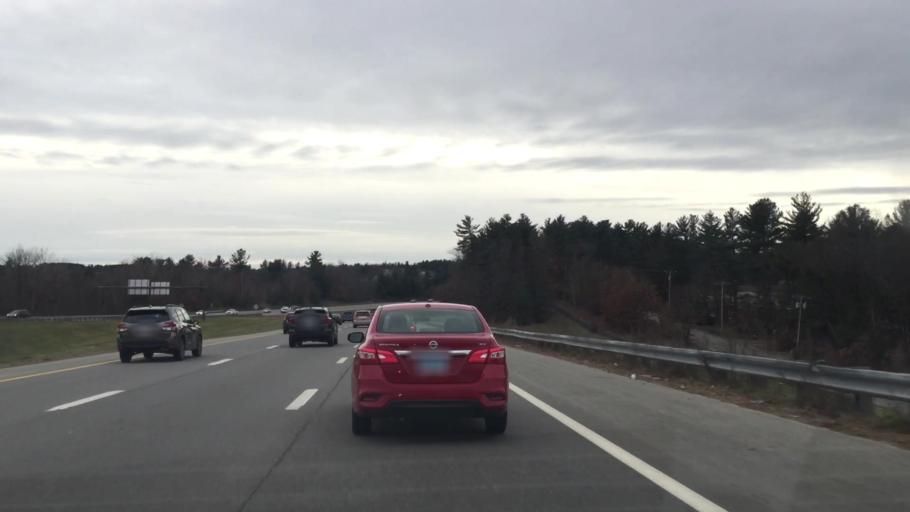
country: US
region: New Hampshire
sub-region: Hillsborough County
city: Hudson
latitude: 42.7275
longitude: -71.4302
